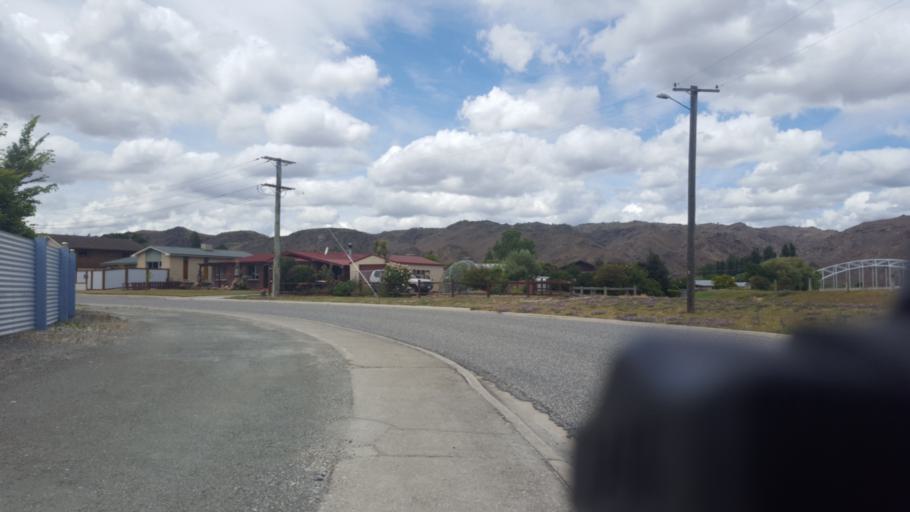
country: NZ
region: Otago
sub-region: Queenstown-Lakes District
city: Wanaka
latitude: -45.2554
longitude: 169.3863
